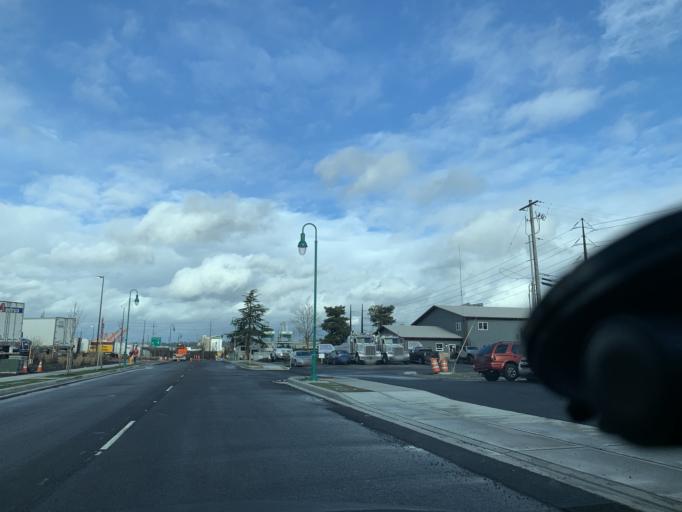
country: US
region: Washington
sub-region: Pierce County
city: Fife
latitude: 47.2442
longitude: -122.3836
